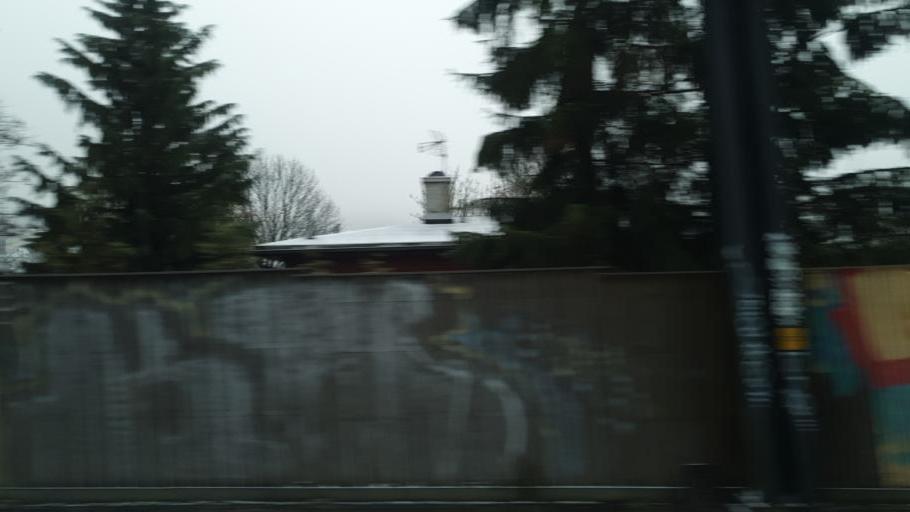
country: NO
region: Akershus
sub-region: Skedsmo
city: Lillestrom
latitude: 59.9504
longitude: 11.0205
